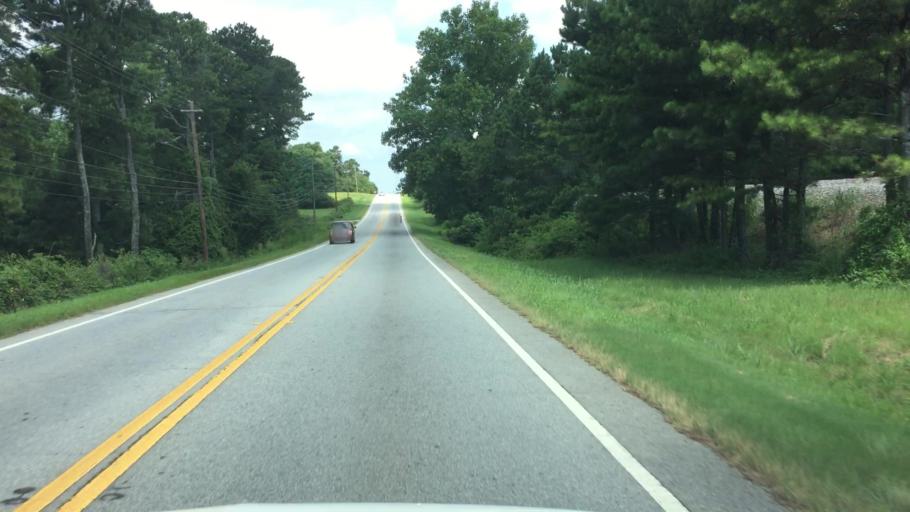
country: US
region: Georgia
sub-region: Barrow County
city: Auburn
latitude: 33.9976
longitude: -83.7915
